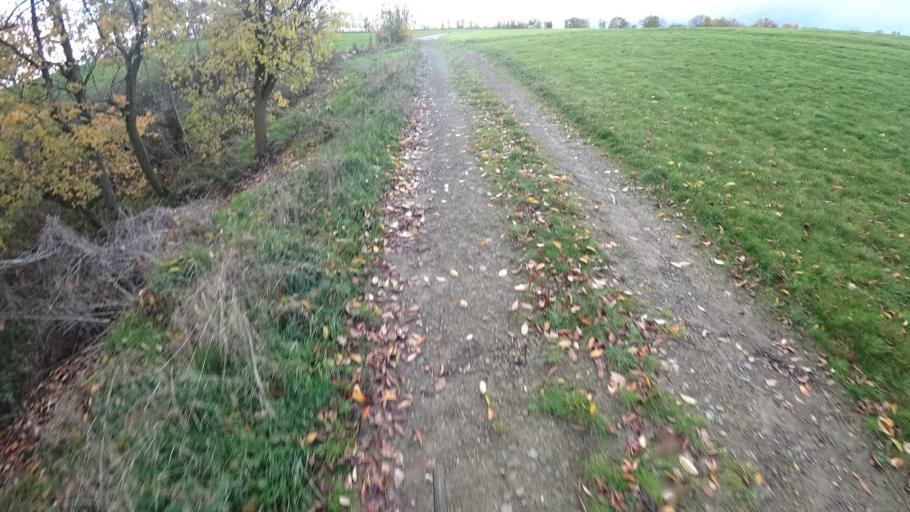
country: DE
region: Rheinland-Pfalz
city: Harscheid
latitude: 50.4629
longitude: 6.8960
